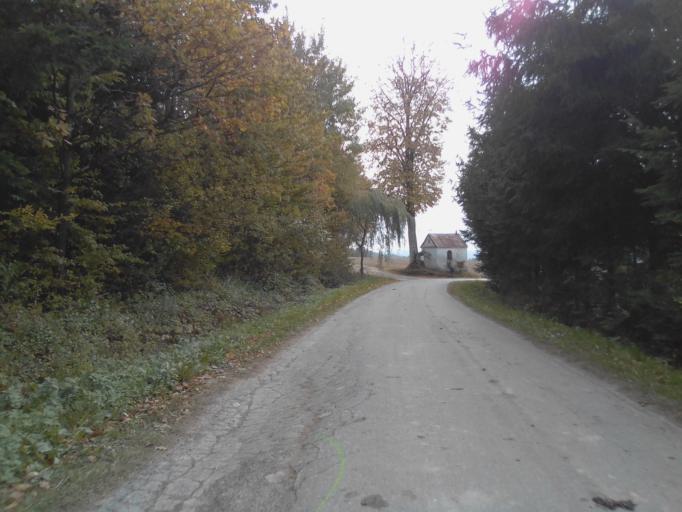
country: PL
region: Subcarpathian Voivodeship
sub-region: Powiat strzyzowski
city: Gwoznica Gorna
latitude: 49.8603
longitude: 21.9751
